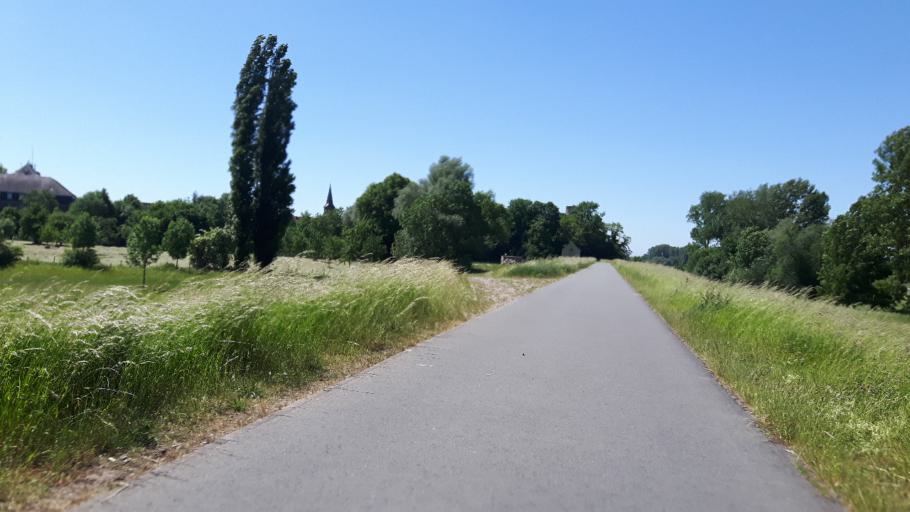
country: DE
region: North Rhine-Westphalia
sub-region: Regierungsbezirk Dusseldorf
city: Meerbusch
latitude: 51.3053
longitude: 6.7386
